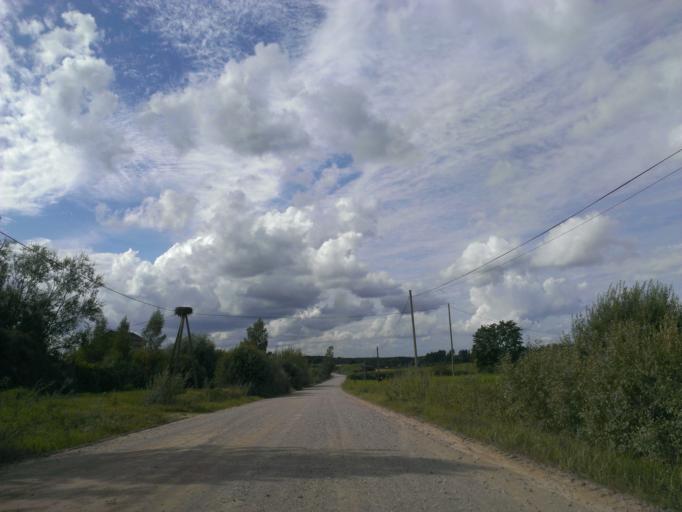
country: LV
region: Skriveri
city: Skriveri
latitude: 56.8435
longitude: 25.1766
